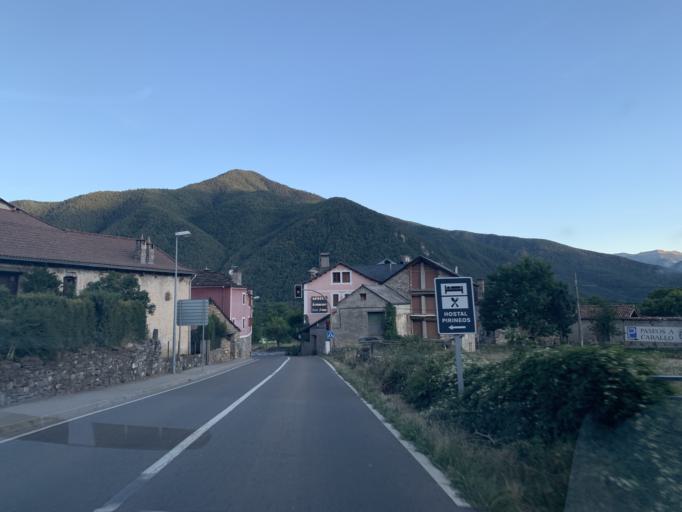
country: ES
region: Aragon
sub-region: Provincia de Huesca
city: Broto
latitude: 42.5789
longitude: -0.1148
